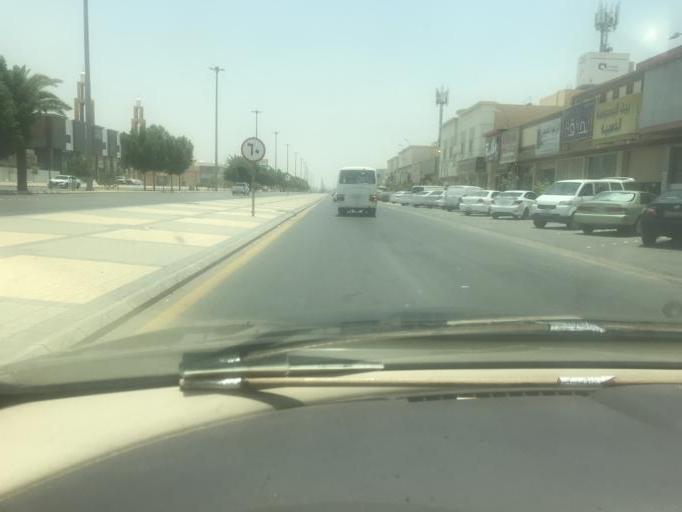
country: SA
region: Ar Riyad
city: Riyadh
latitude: 24.8211
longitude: 46.7510
